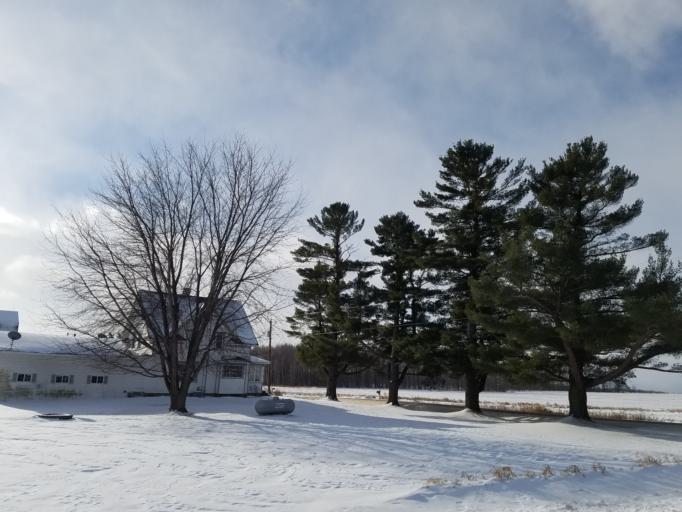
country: US
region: Wisconsin
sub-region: Clark County
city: Loyal
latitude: 44.6399
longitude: -90.4167
